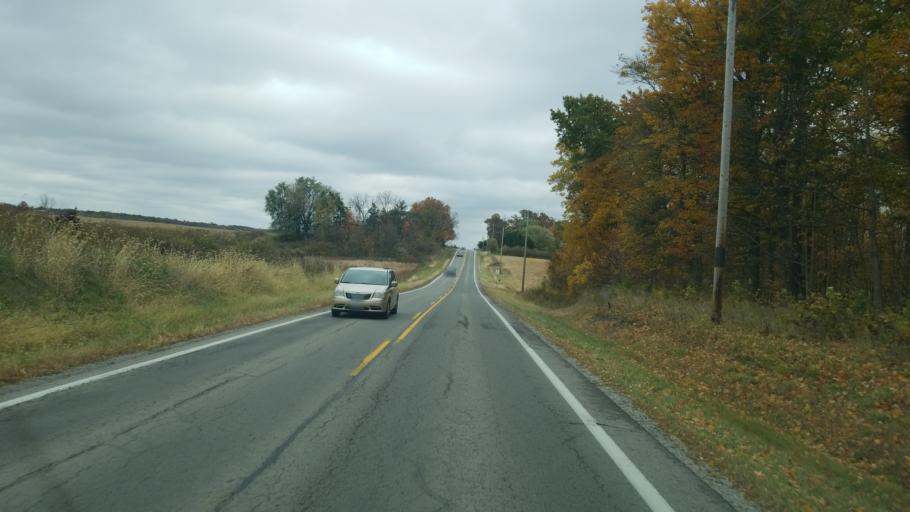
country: US
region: Ohio
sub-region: Seneca County
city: Tiffin
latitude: 41.0812
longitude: -83.0052
